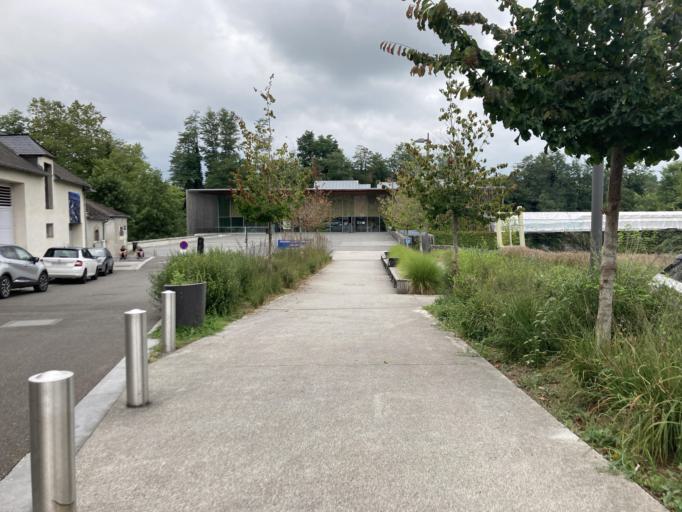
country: FR
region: Aquitaine
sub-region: Departement des Pyrenees-Atlantiques
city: Oloron-Sainte-Marie
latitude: 43.1932
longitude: -0.6076
